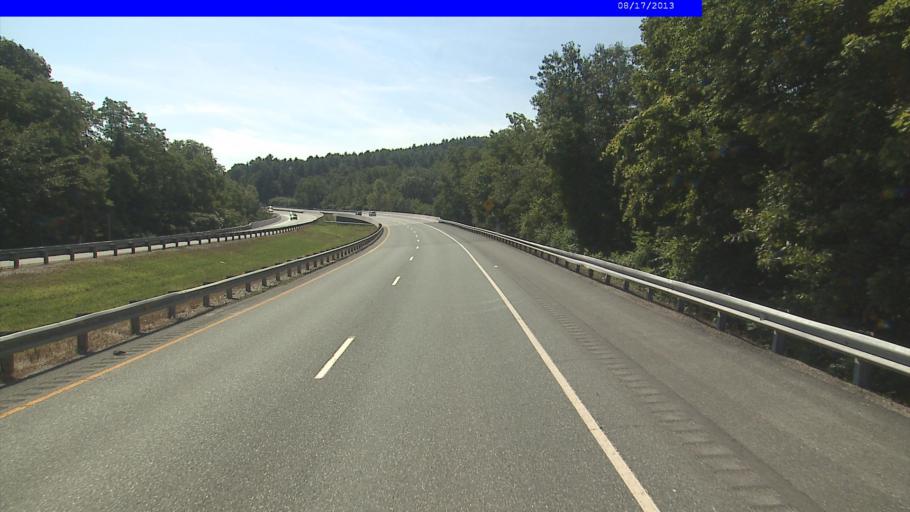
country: US
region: Vermont
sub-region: Windham County
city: Brattleboro
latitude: 42.8502
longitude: -72.5794
